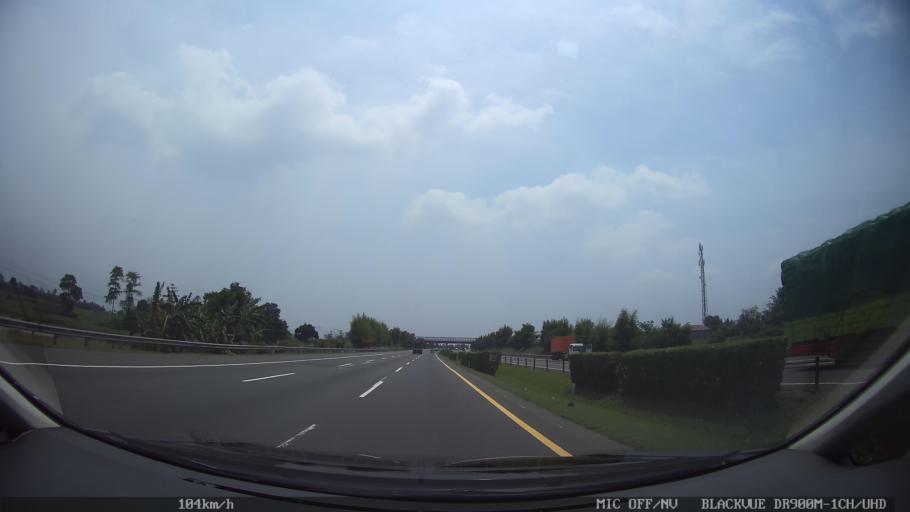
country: ID
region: West Java
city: Kresek
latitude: -6.1772
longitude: 106.3622
